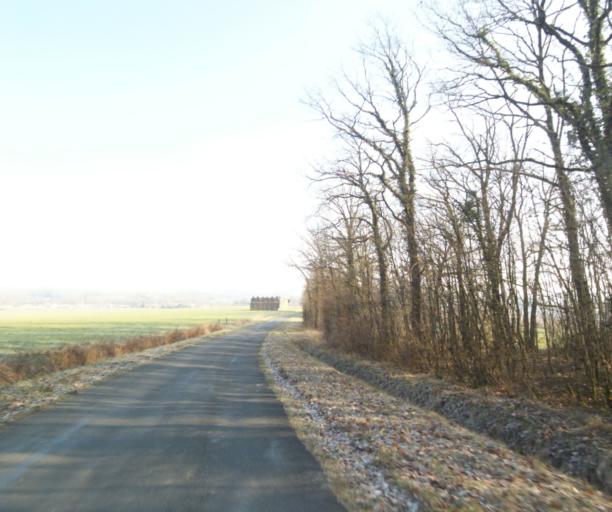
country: FR
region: Champagne-Ardenne
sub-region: Departement de la Haute-Marne
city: Wassy
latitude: 48.4697
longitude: 4.9565
